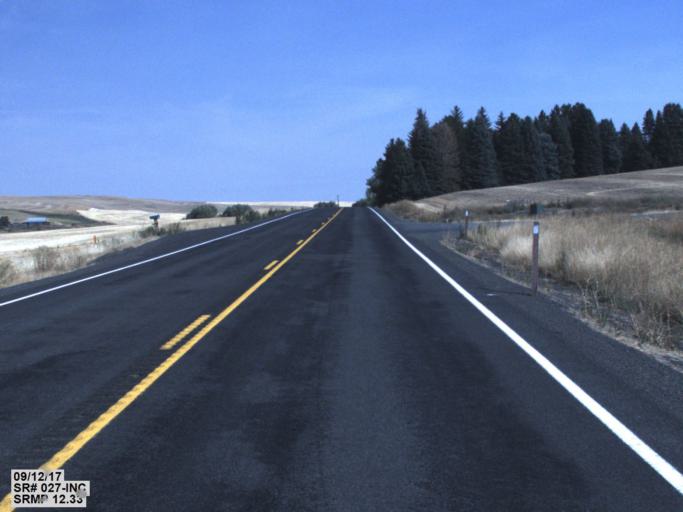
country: US
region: Washington
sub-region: Whitman County
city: Pullman
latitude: 46.8878
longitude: -117.1199
